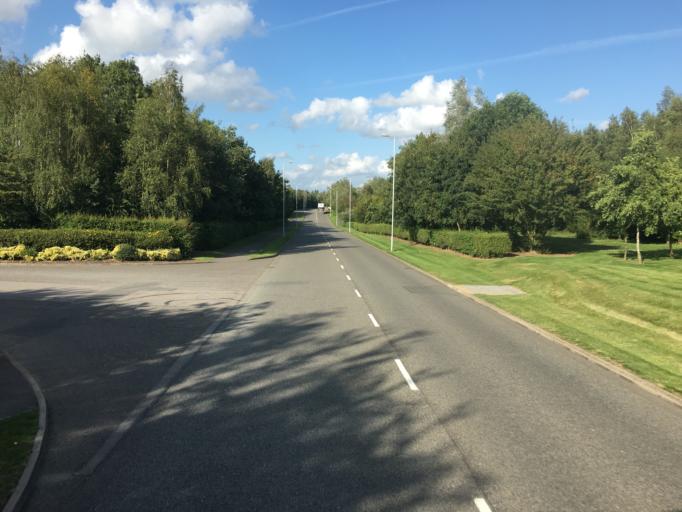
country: GB
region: England
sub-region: Leicestershire
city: Lutterworth
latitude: 52.4614
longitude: -1.2395
